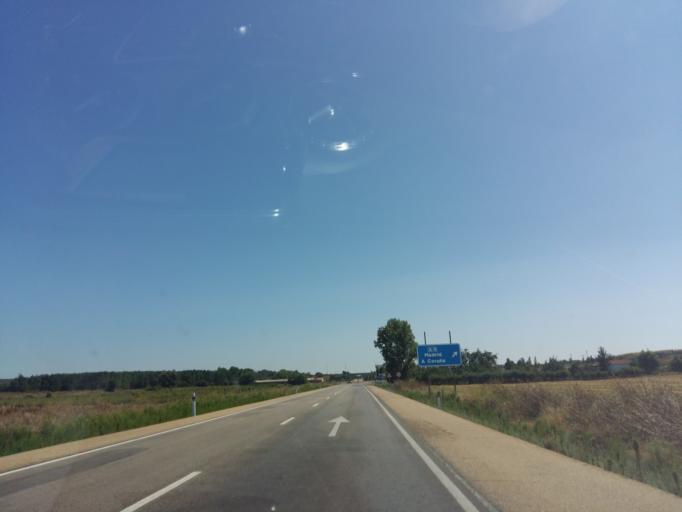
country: ES
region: Castille and Leon
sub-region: Provincia de Leon
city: Astorga
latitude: 42.4430
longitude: -6.0420
